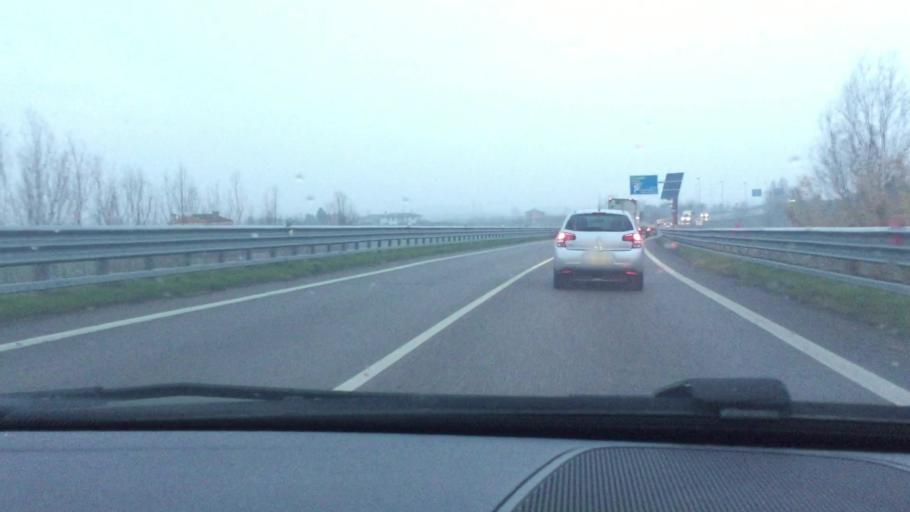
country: IT
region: Veneto
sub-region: Provincia di Padova
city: Piove di Sacco-Piovega
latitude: 45.3103
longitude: 12.0391
